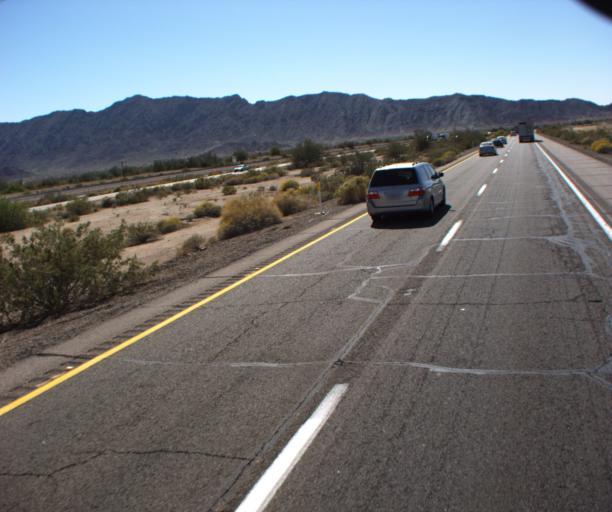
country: US
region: Arizona
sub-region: Yuma County
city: Wellton
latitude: 32.7342
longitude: -113.7060
